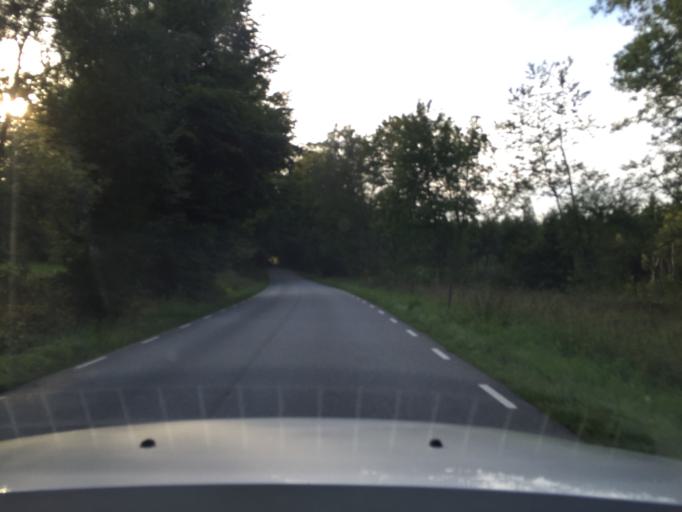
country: SE
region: Skane
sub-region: Hassleholms Kommun
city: Sosdala
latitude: 56.0479
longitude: 13.6531
